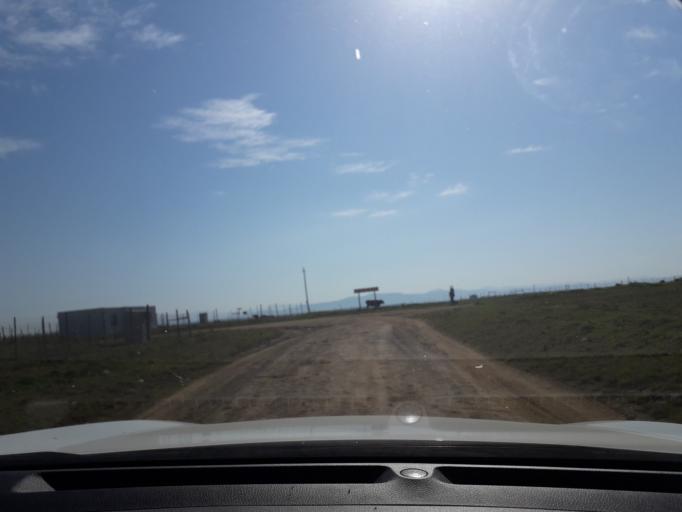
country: ZA
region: Eastern Cape
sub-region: Buffalo City Metropolitan Municipality
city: Bhisho
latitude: -32.9718
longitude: 27.3183
